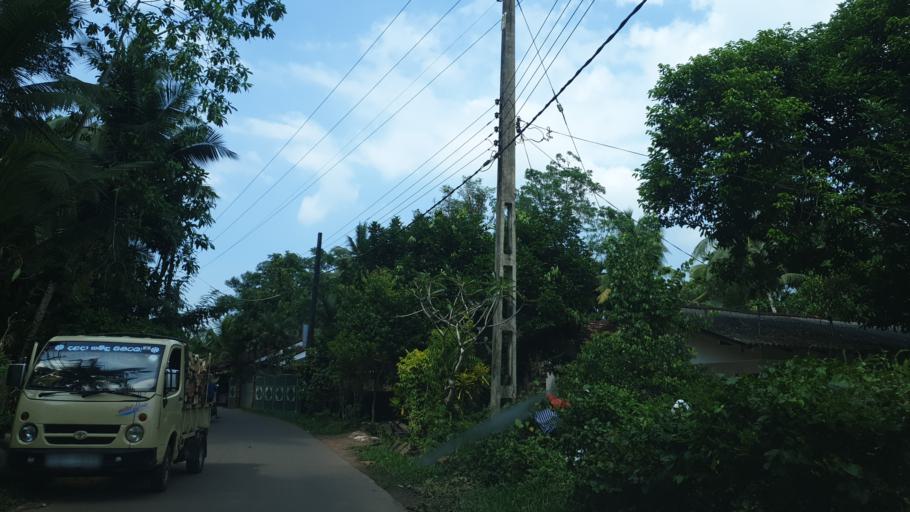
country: LK
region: Western
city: Panadura
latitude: 6.7343
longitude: 79.9526
